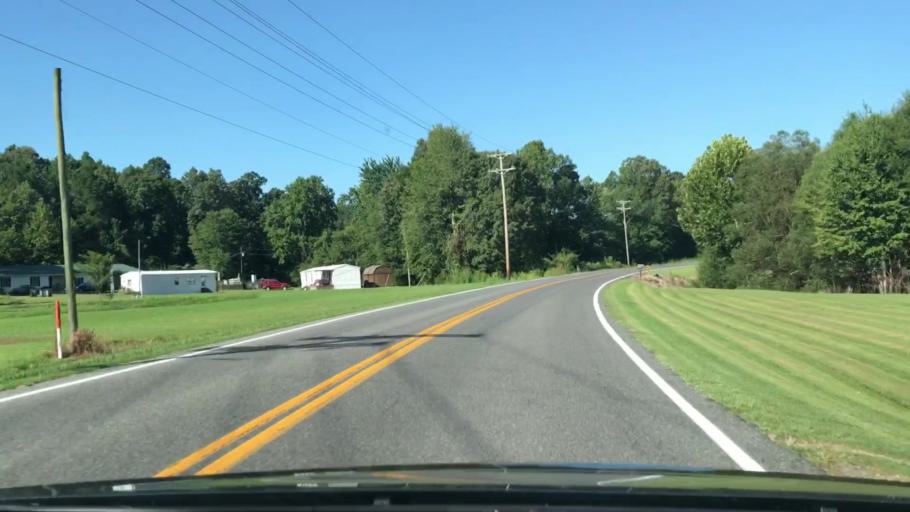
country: US
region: Kentucky
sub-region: Marshall County
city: Benton
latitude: 36.7747
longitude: -88.4817
